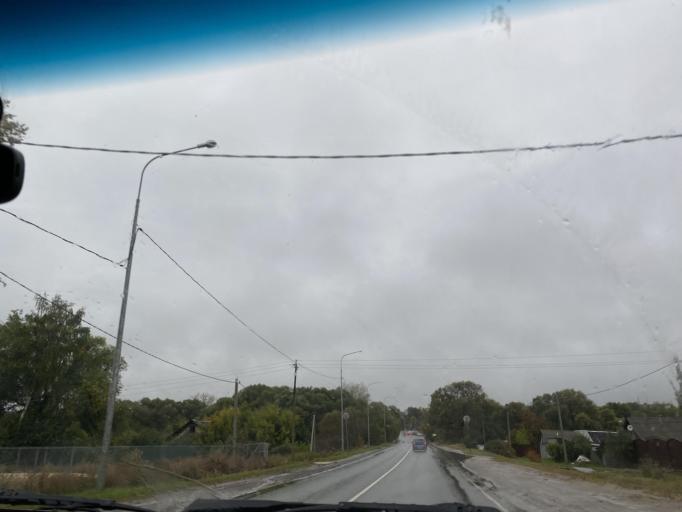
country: RU
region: Rjazan
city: Starozhilovo
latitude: 54.4407
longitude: 39.8959
